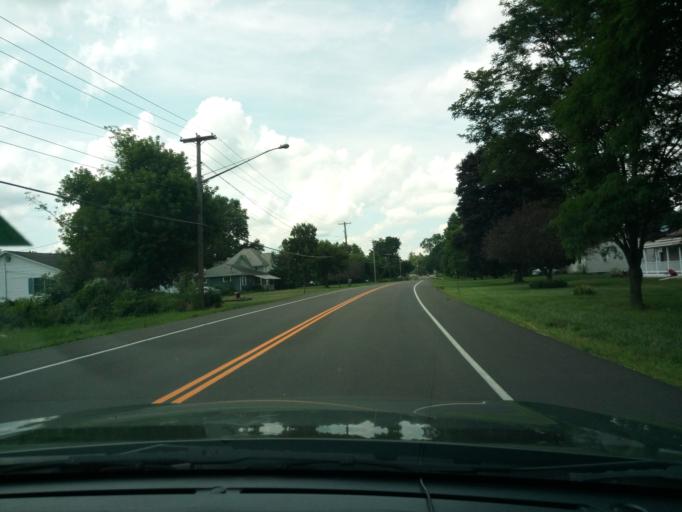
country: US
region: New York
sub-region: Chemung County
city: Southport
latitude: 42.0529
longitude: -76.7797
